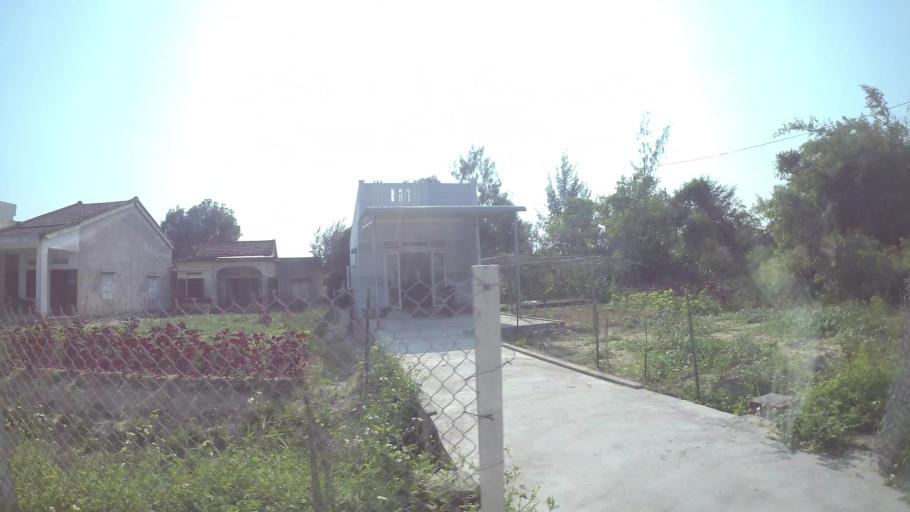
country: VN
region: Da Nang
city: Ngu Hanh Son
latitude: 15.9549
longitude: 108.2654
